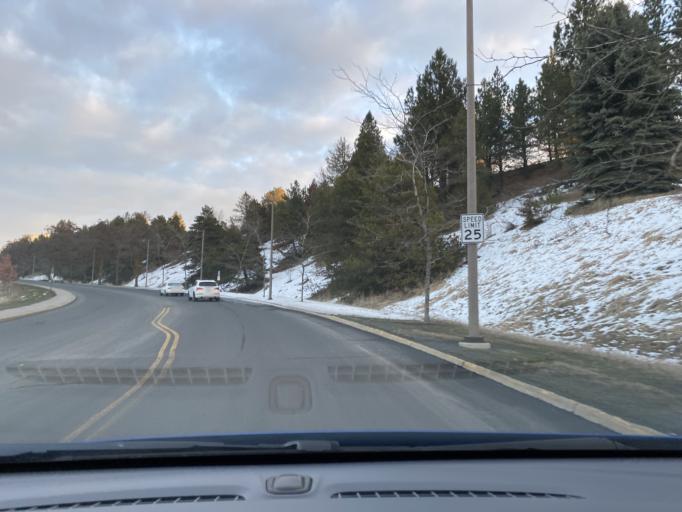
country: US
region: Idaho
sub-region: Latah County
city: Moscow
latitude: 46.7260
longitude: -117.0228
